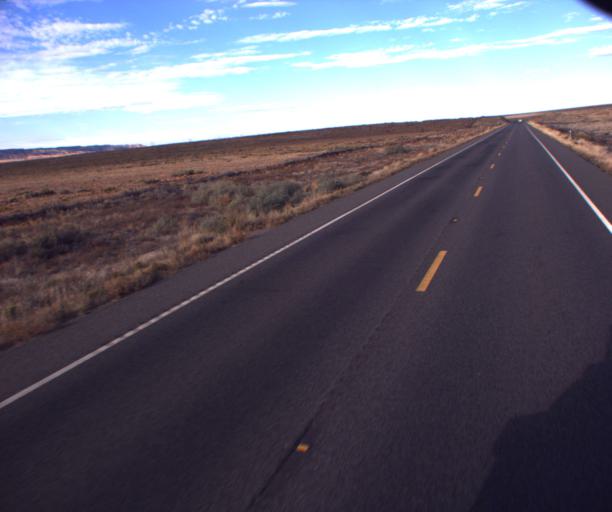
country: US
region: Arizona
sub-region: Apache County
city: Lukachukai
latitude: 36.9539
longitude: -109.2936
